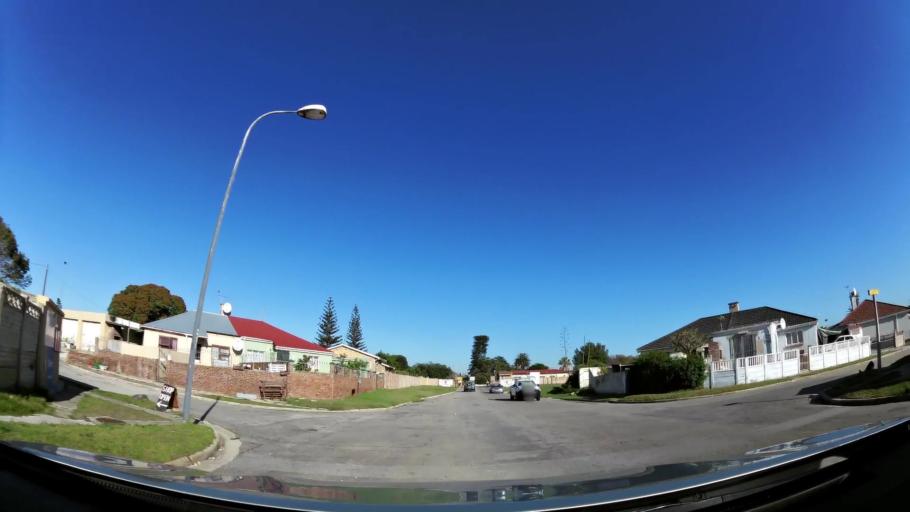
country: ZA
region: Eastern Cape
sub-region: Nelson Mandela Bay Metropolitan Municipality
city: Port Elizabeth
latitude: -33.9824
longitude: 25.6287
